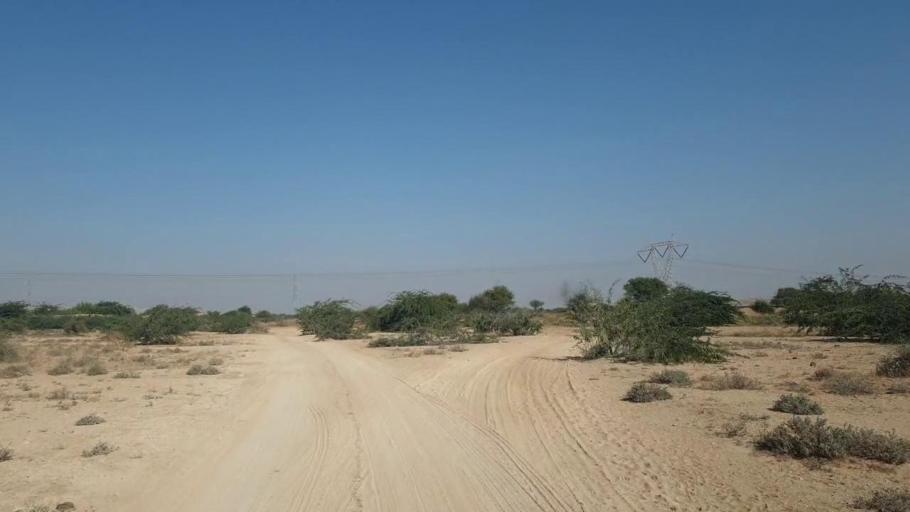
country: PK
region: Sindh
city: Gharo
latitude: 25.1869
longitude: 67.7381
